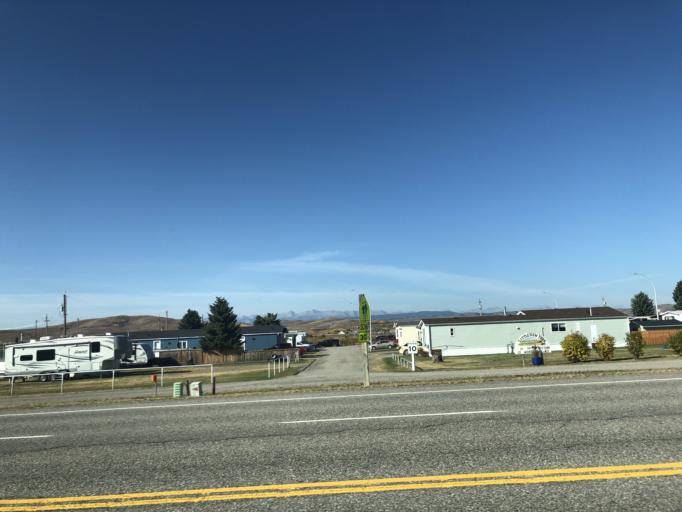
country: CA
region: Alberta
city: Black Diamond
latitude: 50.5362
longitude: -114.2309
